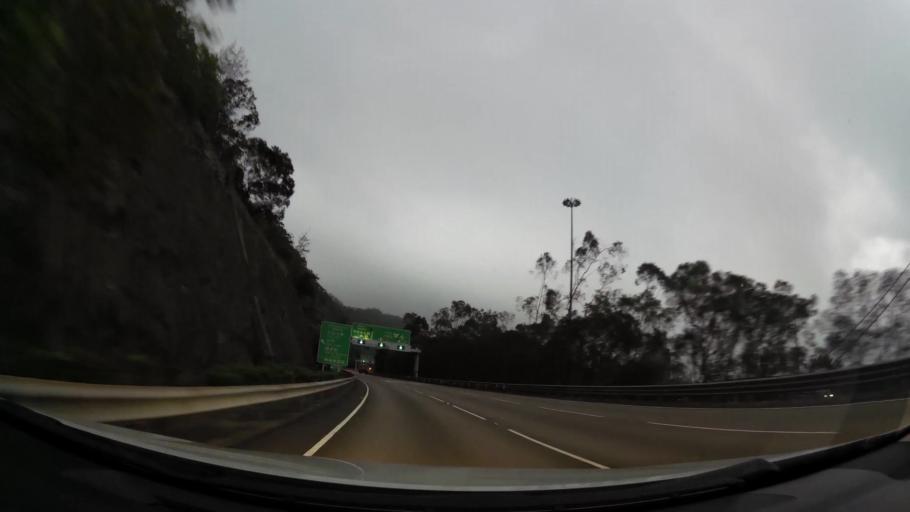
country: HK
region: Tsuen Wan
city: Tsuen Wan
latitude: 22.3568
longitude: 114.0840
